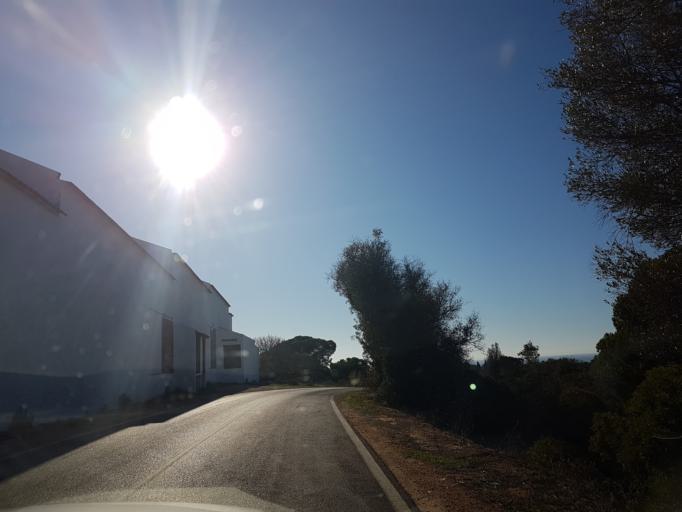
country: PT
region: Faro
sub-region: Lagoa
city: Carvoeiro
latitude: 37.1013
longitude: -8.4161
